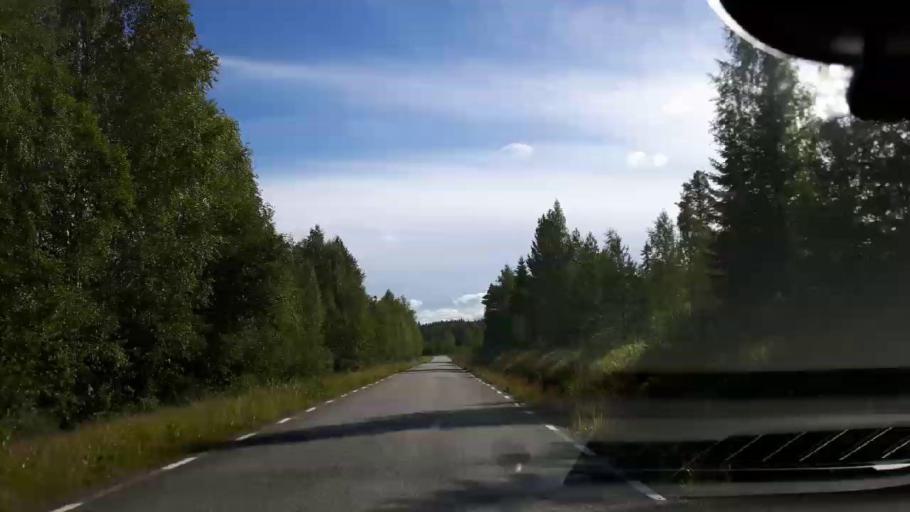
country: SE
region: Jaemtland
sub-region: OEstersunds Kommun
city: Lit
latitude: 63.2286
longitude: 15.2698
